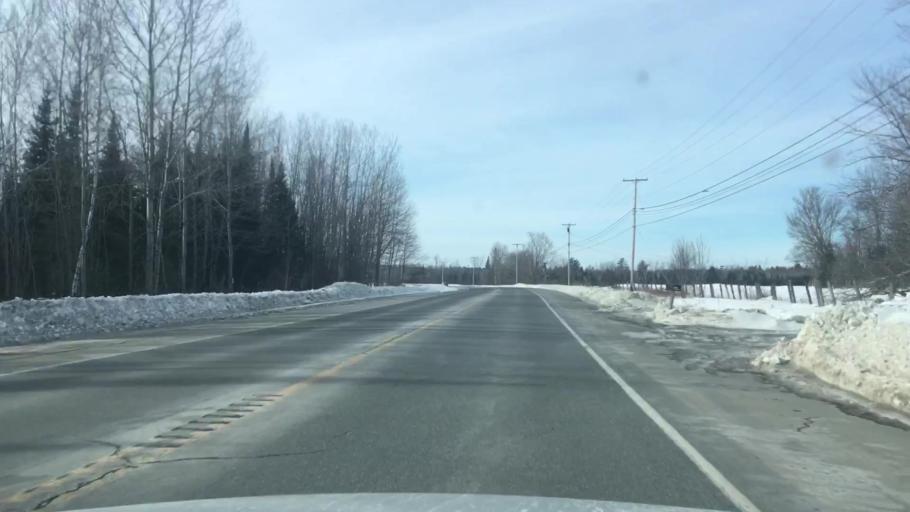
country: US
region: Maine
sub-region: Penobscot County
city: Kenduskeag
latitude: 44.9085
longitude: -68.8955
